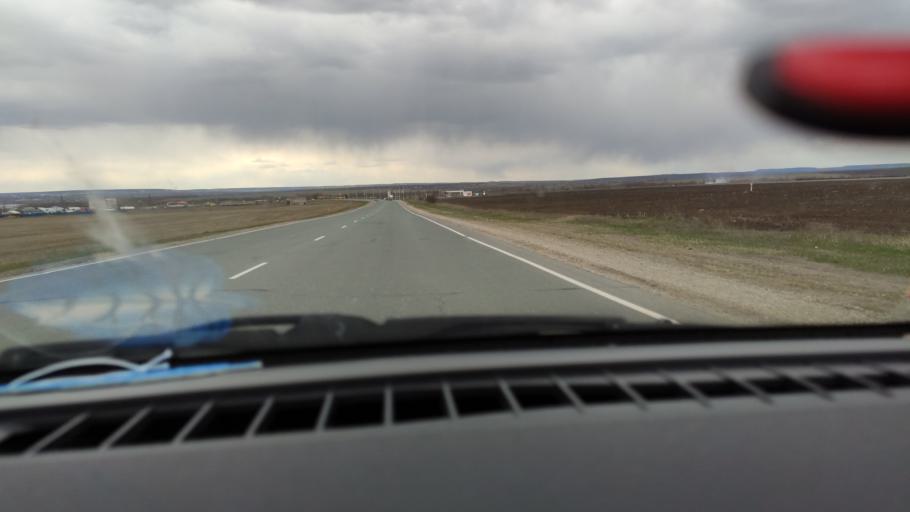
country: RU
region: Saratov
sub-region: Saratovskiy Rayon
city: Saratov
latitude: 51.7365
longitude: 46.0382
